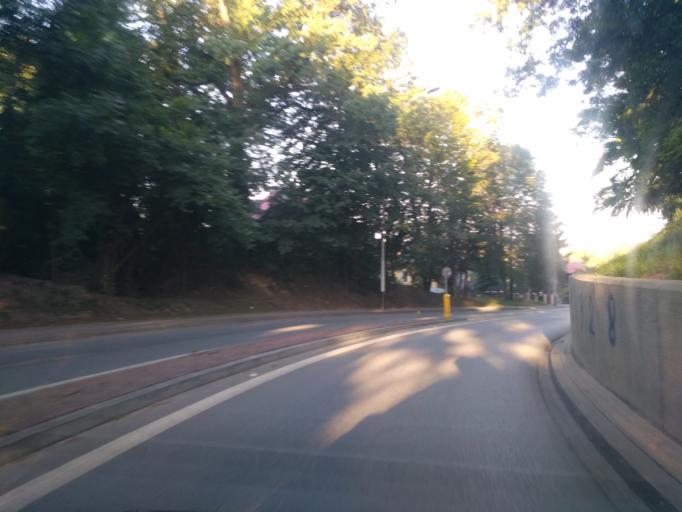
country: PL
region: Subcarpathian Voivodeship
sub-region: Krosno
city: Krosno
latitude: 49.6959
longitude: 21.7788
